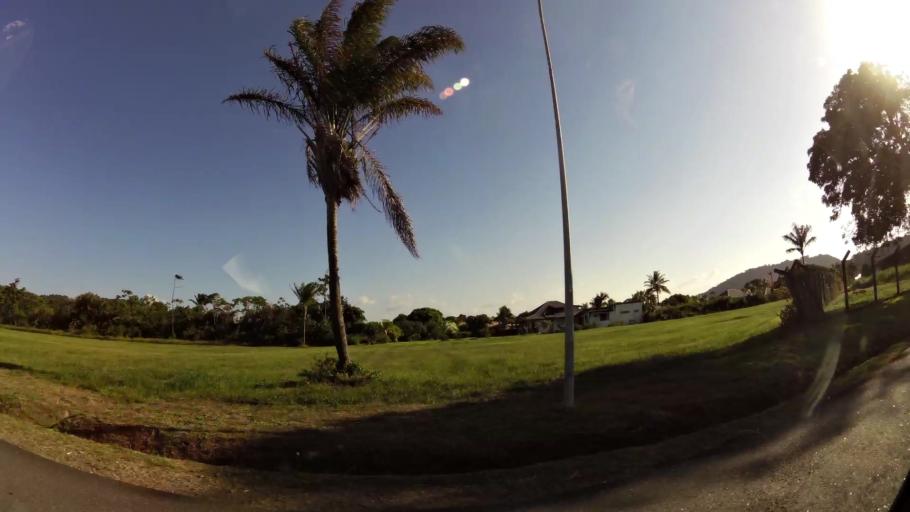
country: GF
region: Guyane
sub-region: Guyane
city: Remire-Montjoly
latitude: 4.9011
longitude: -52.2771
